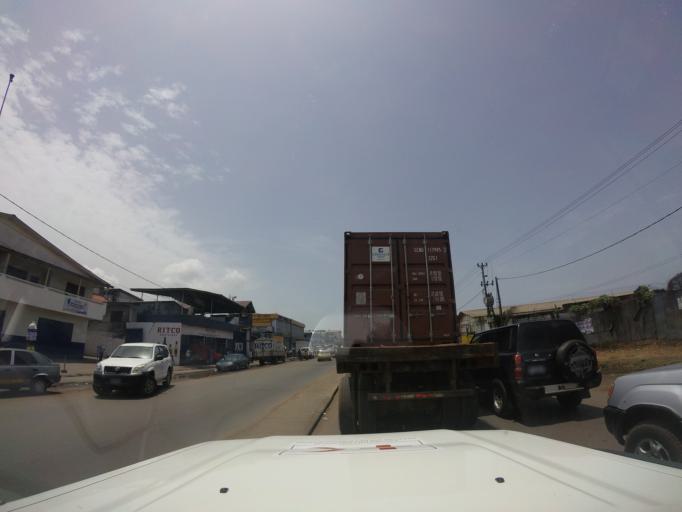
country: LR
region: Montserrado
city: Monrovia
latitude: 6.3313
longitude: -10.7990
